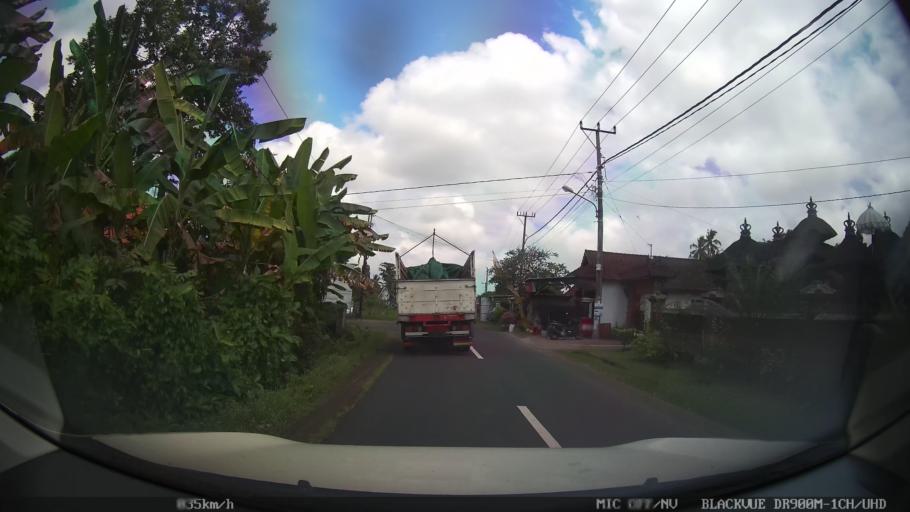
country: ID
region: Bali
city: Banjar Kelodan
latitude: -8.5183
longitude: 115.3648
